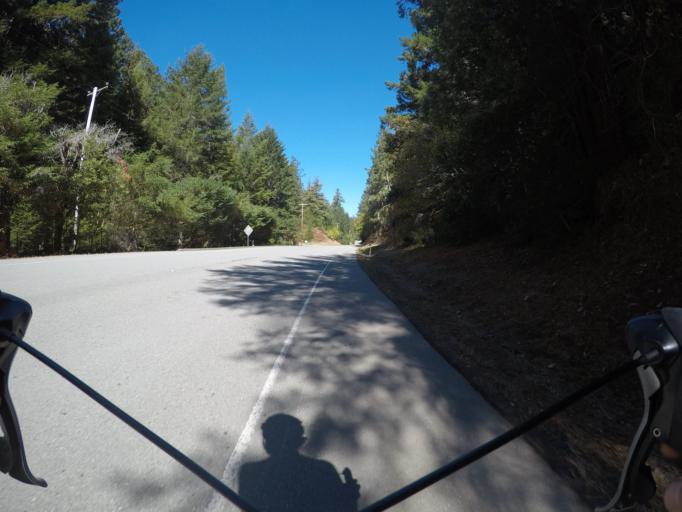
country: US
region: California
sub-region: San Mateo County
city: Portola Valley
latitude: 37.3011
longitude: -122.2662
